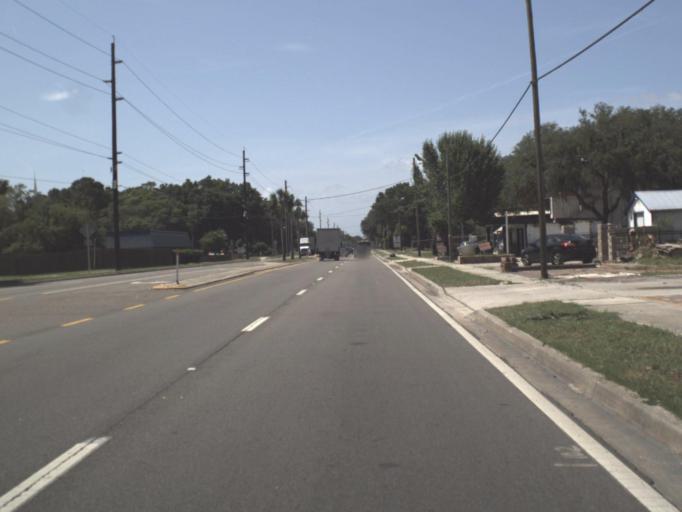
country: US
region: Florida
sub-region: Nassau County
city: Fernandina Beach
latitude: 30.6534
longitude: -81.4607
